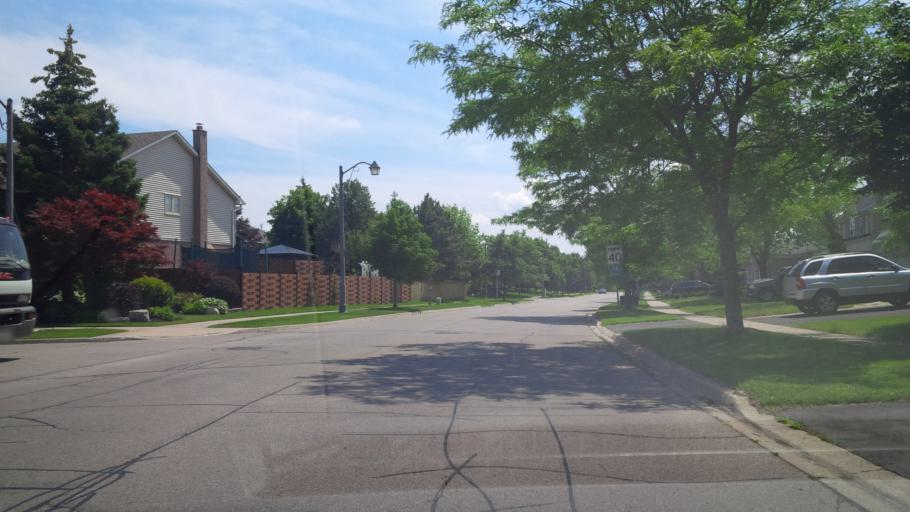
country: CA
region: Ontario
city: Burlington
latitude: 43.3939
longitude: -79.7998
